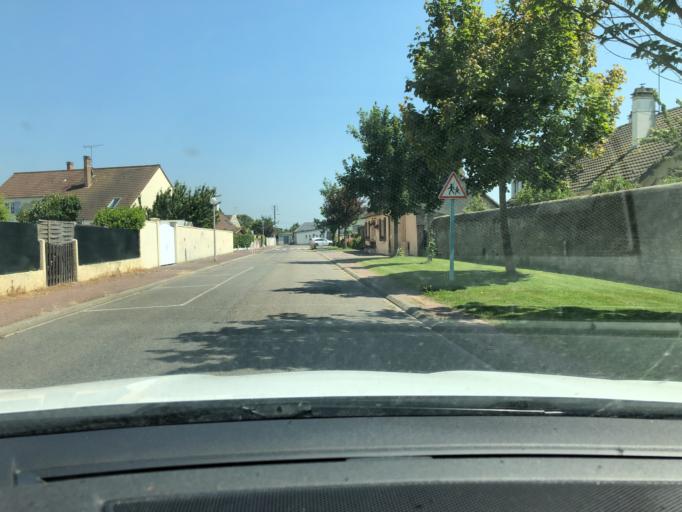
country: FR
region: Lower Normandy
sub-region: Departement du Calvados
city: Lion-sur-Mer
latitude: 49.3021
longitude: -0.3248
